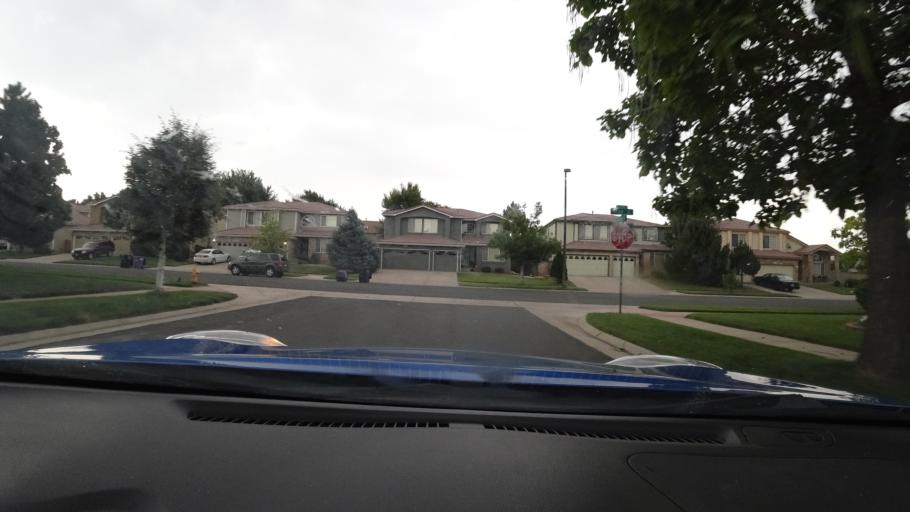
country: US
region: Colorado
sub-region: Adams County
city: Aurora
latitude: 39.7754
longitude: -104.7523
